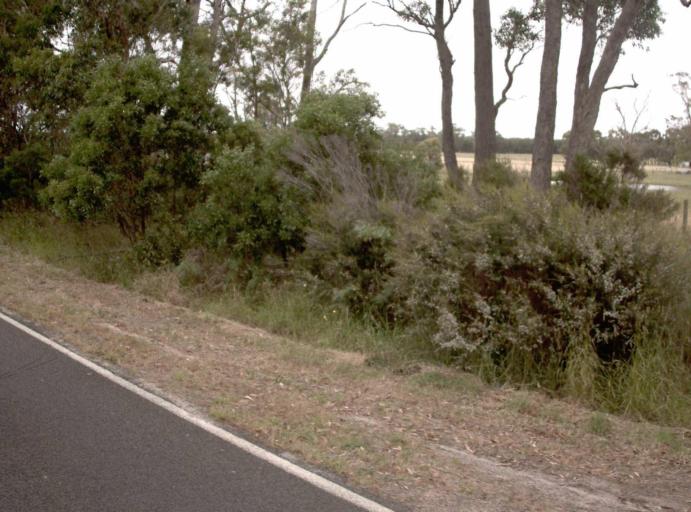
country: AU
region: Victoria
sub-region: Latrobe
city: Traralgon
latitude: -38.5175
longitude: 146.8579
